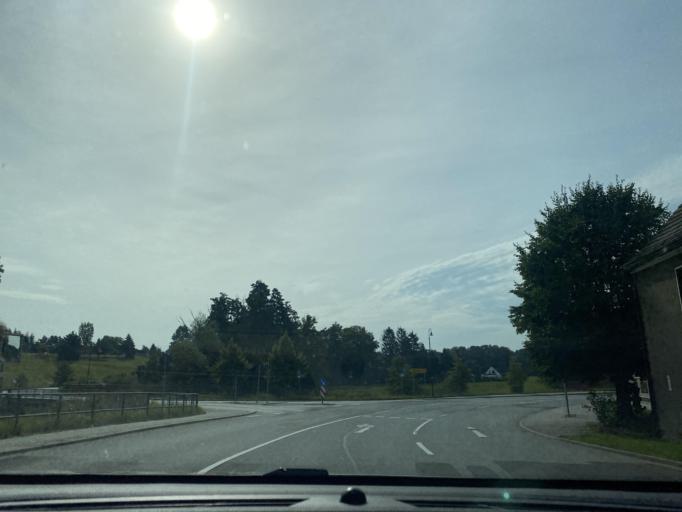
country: DE
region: Saxony
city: Reichenbach
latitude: 51.1949
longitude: 14.7560
